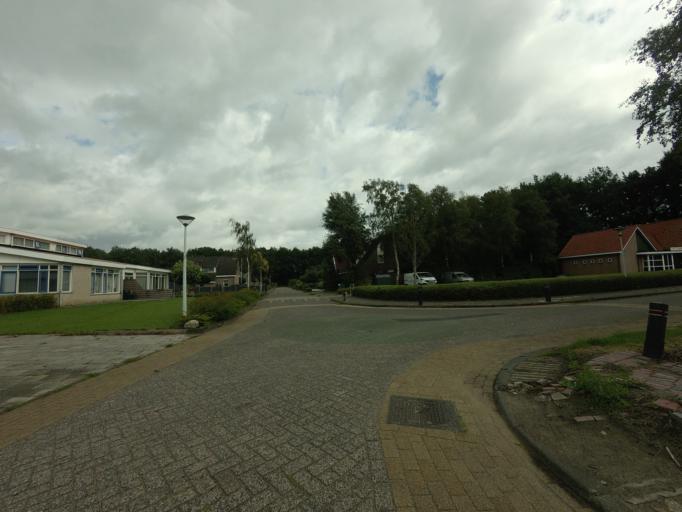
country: NL
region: Drenthe
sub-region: Gemeente Westerveld
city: Dwingeloo
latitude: 52.9652
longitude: 6.2887
